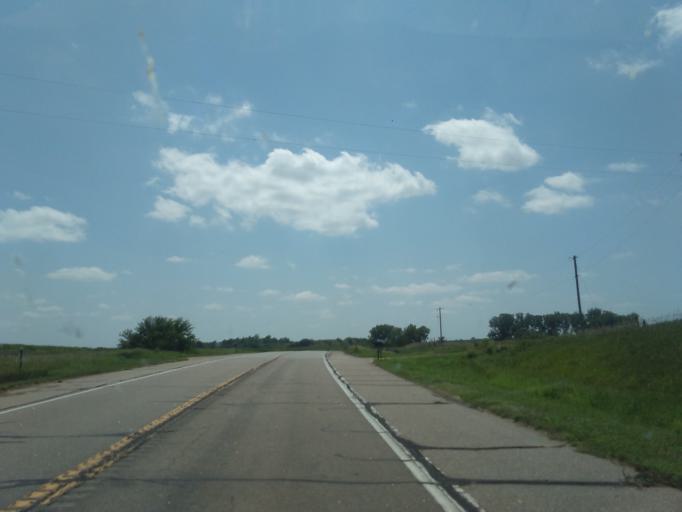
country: US
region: Nebraska
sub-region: Dawson County
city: Lexington
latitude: 40.7001
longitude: -99.7901
